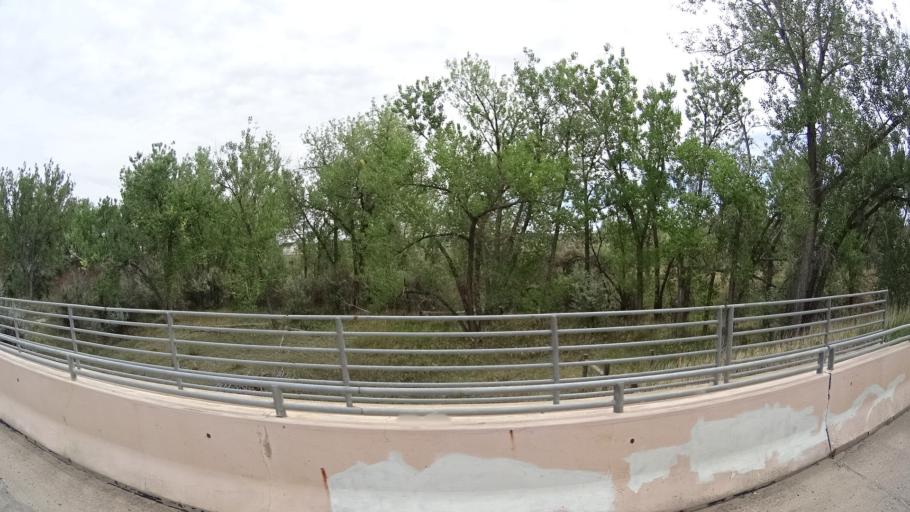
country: US
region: Colorado
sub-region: El Paso County
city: Fountain
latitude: 38.6729
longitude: -104.6963
